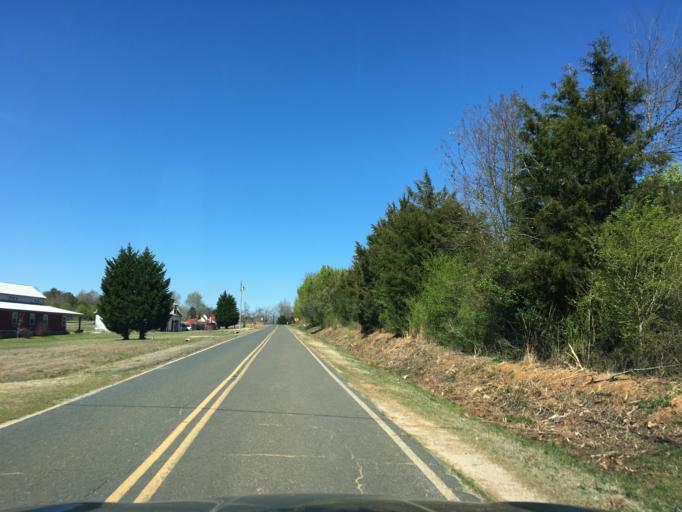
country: US
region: South Carolina
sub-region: Spartanburg County
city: Woodruff
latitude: 34.8265
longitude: -82.0795
